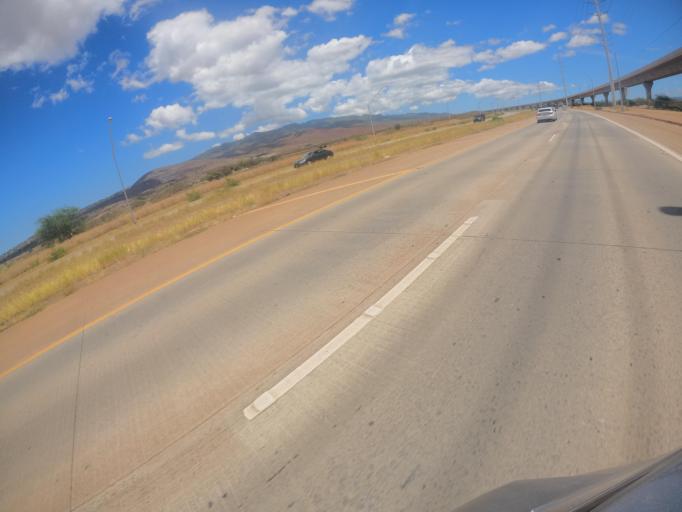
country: US
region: Hawaii
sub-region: Honolulu County
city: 'Ewa Villages
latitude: 21.3494
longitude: -158.0484
